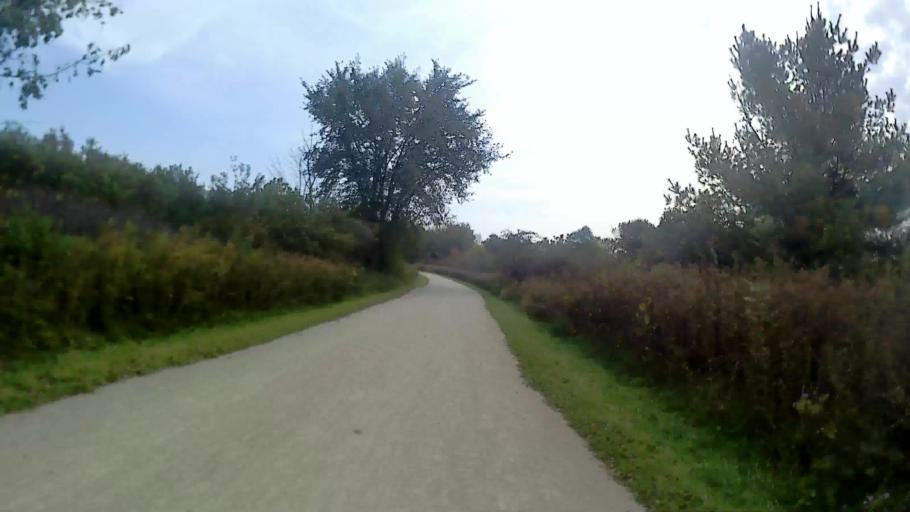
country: US
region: Illinois
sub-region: DuPage County
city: Warrenville
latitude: 41.8166
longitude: -88.1461
